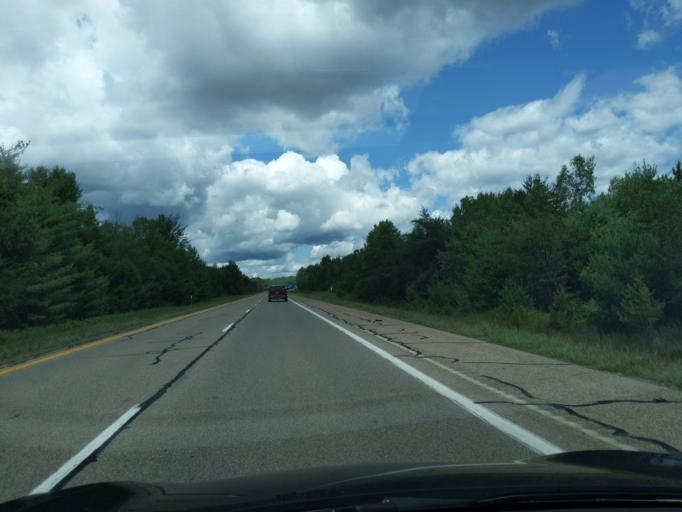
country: US
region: Michigan
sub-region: Roscommon County
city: Houghton Lake
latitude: 44.3045
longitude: -84.8028
